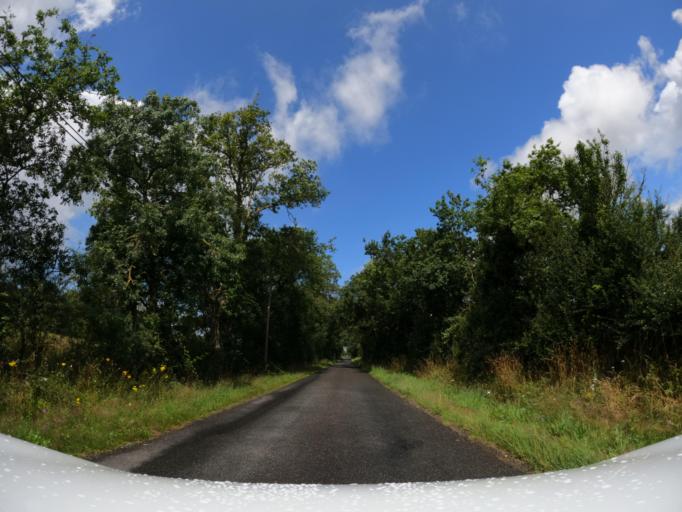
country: FR
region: Pays de la Loire
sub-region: Departement de la Loire-Atlantique
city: Saint-Mars-du-Desert
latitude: 47.3845
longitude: -1.3920
